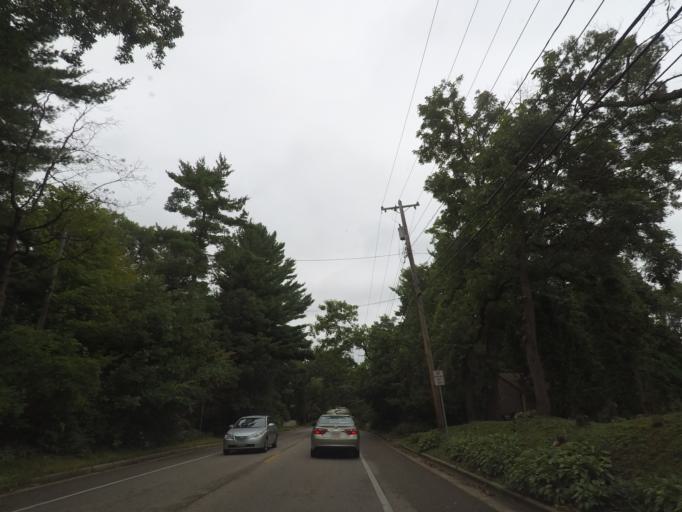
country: US
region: Wisconsin
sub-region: Dane County
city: Shorewood Hills
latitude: 43.0412
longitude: -89.4734
